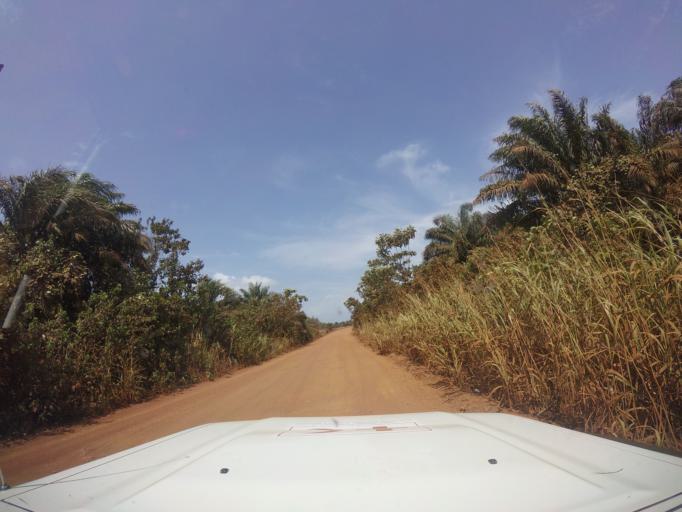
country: LR
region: Grand Cape Mount
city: Robertsport
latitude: 6.7479
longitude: -11.3488
